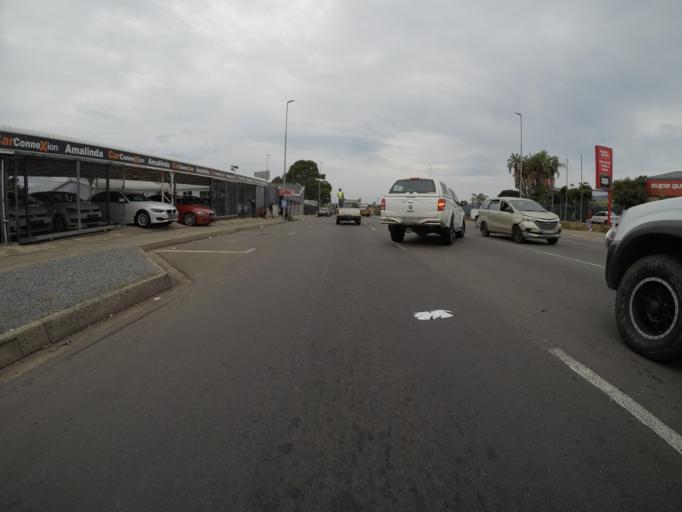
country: ZA
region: Eastern Cape
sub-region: Buffalo City Metropolitan Municipality
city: East London
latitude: -32.9969
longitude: 27.8749
